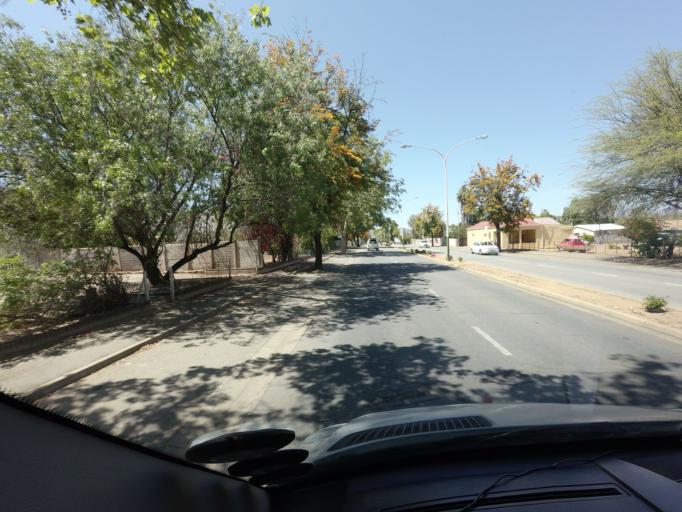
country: ZA
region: Western Cape
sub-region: Eden District Municipality
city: Oudtshoorn
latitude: -33.6038
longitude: 22.2093
